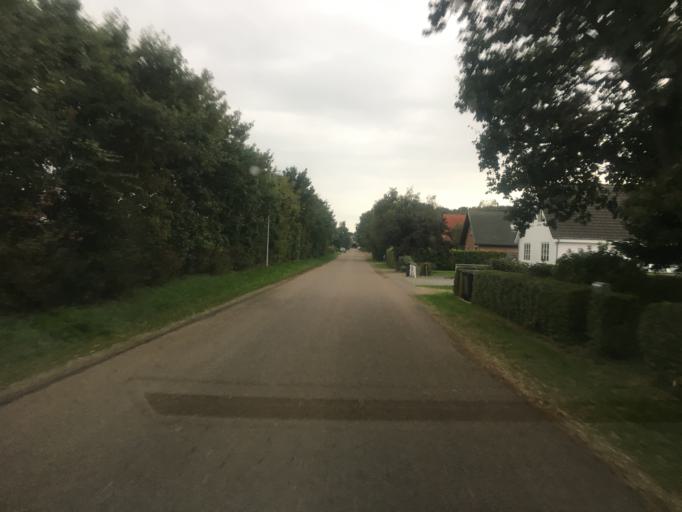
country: DE
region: Schleswig-Holstein
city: Ellhoft
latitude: 54.9493
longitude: 8.9724
